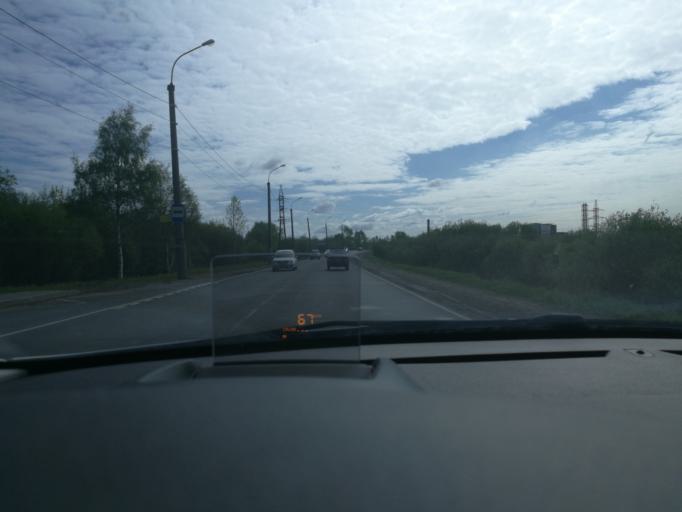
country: RU
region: Arkhangelskaya
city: Arkhangel'sk
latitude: 64.5975
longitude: 40.5373
